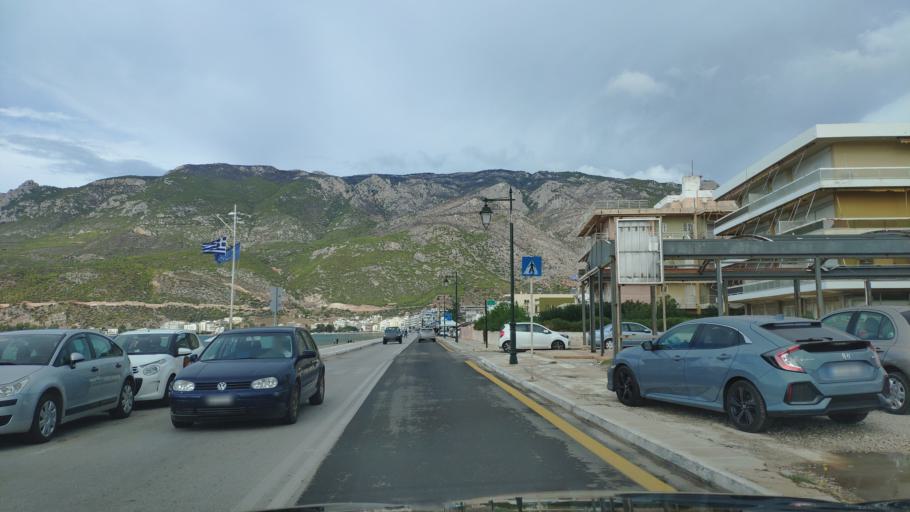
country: GR
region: Peloponnese
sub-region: Nomos Korinthias
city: Loutraki
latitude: 37.9662
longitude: 22.9718
